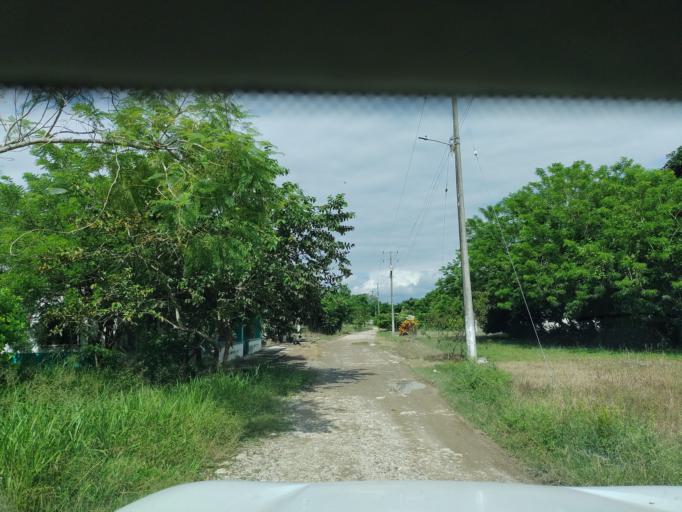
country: MX
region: Veracruz
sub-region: Atzalan
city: Colonias Pedernales
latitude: 20.0415
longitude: -97.0760
